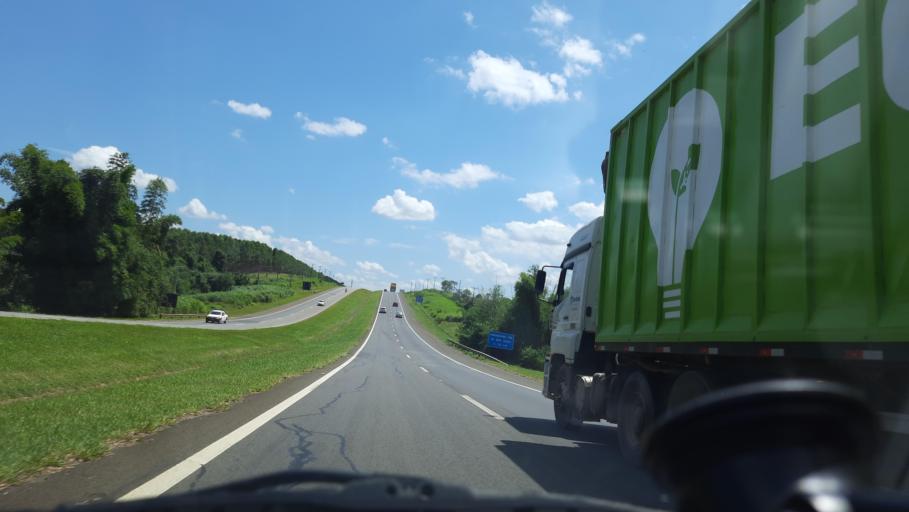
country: BR
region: Sao Paulo
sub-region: Moji-Guacu
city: Mogi-Gaucu
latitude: -22.3358
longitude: -46.9589
